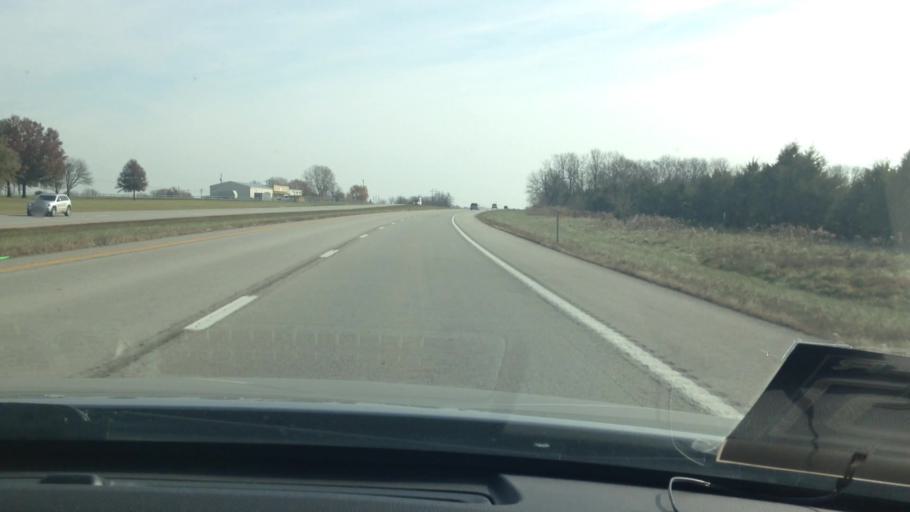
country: US
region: Missouri
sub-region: Cass County
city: Garden City
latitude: 38.6001
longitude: -94.2600
